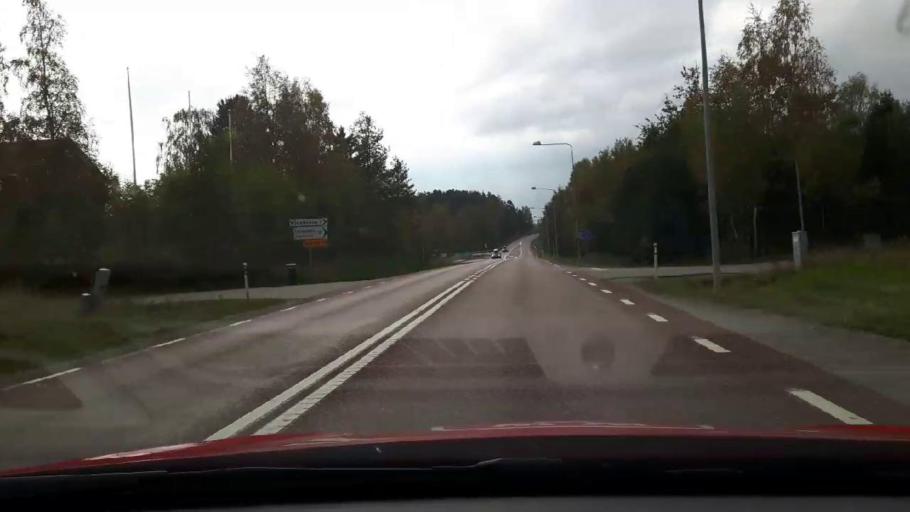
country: SE
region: Gaevleborg
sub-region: Bollnas Kommun
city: Kilafors
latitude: 61.2530
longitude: 16.5518
